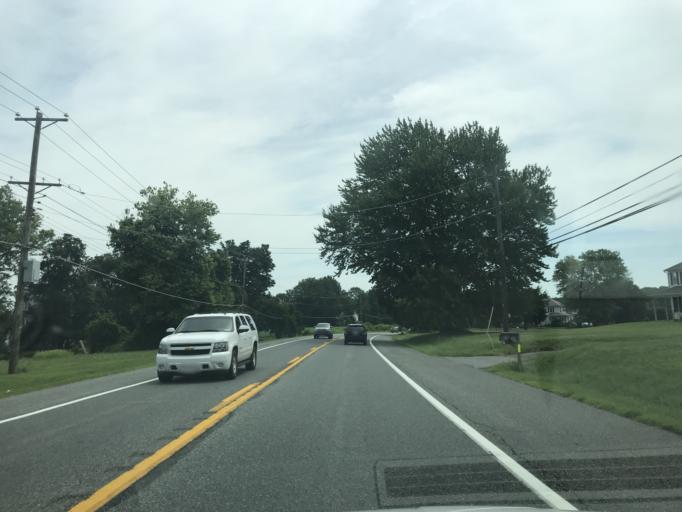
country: US
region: Maryland
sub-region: Harford County
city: Aberdeen
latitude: 39.6513
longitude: -76.2142
